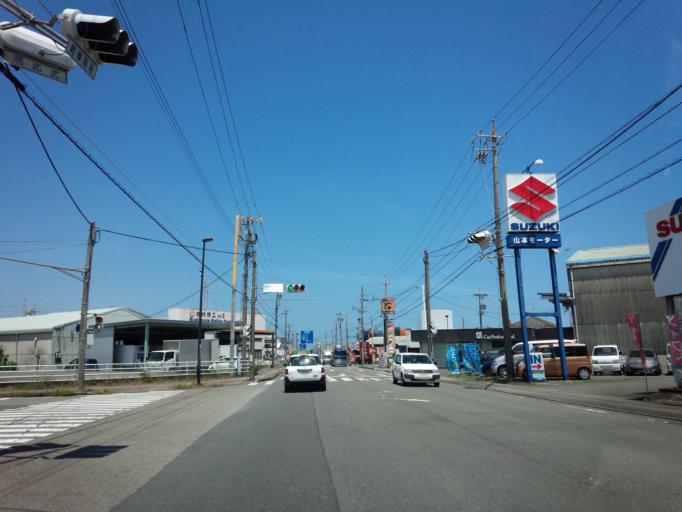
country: JP
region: Shizuoka
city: Yaizu
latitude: 34.8279
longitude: 138.2981
